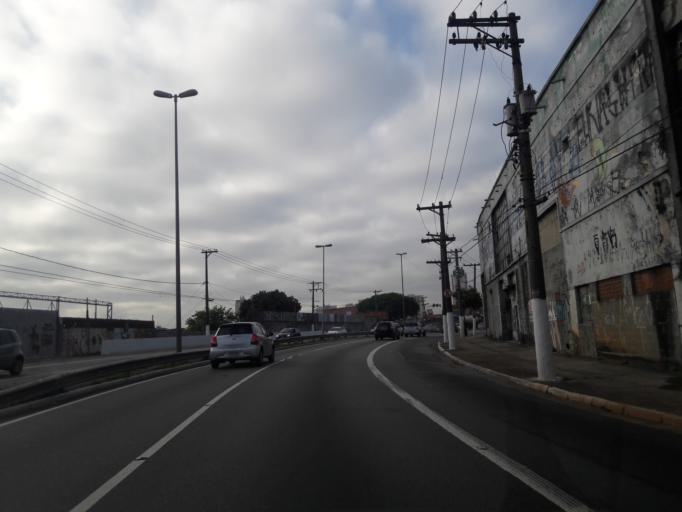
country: BR
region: Sao Paulo
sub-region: Sao Caetano Do Sul
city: Sao Caetano do Sul
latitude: -23.6063
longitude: -46.5994
